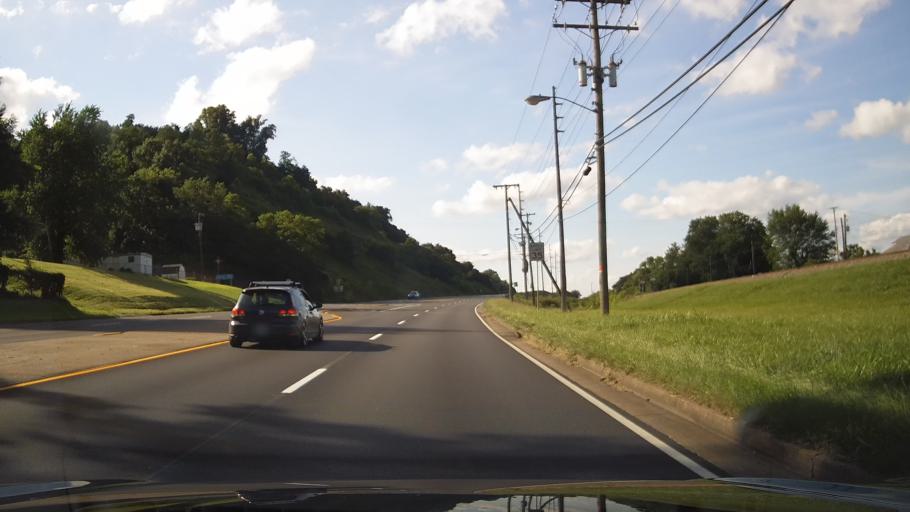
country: US
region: Ohio
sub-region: Lawrence County
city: South Point
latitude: 38.4203
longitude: -82.6010
